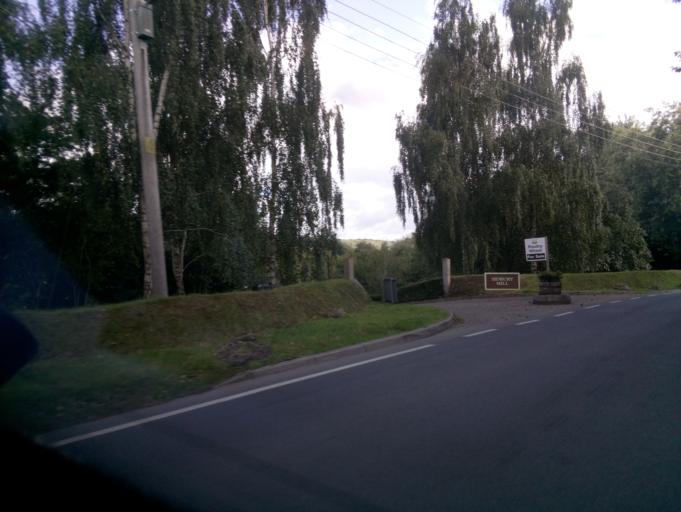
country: GB
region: England
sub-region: Devon
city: Sidmouth
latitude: 50.7153
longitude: -3.2229
